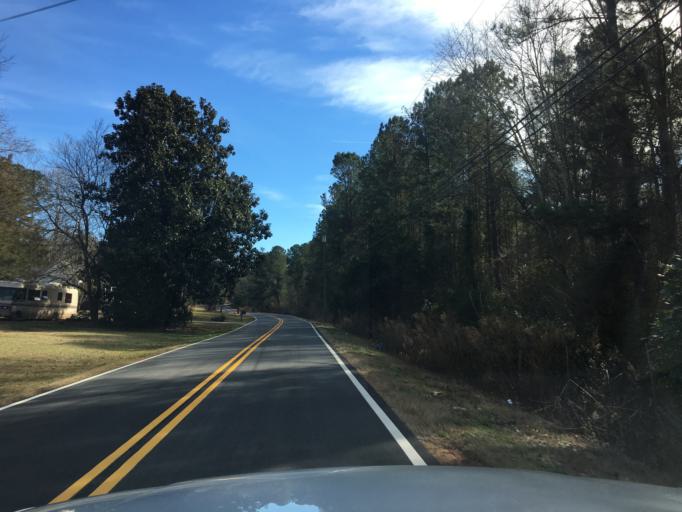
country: US
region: Georgia
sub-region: Rockdale County
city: Lakeview Estates
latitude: 33.7361
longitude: -84.0324
